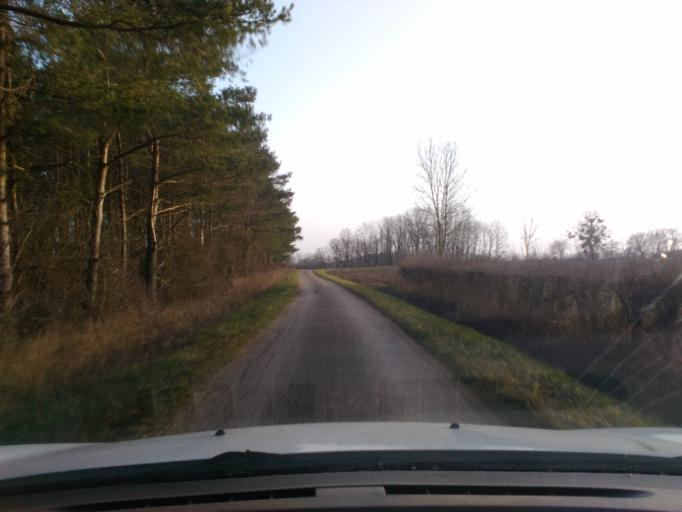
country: FR
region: Lorraine
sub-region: Departement des Vosges
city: Vittel
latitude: 48.2621
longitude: 6.0017
